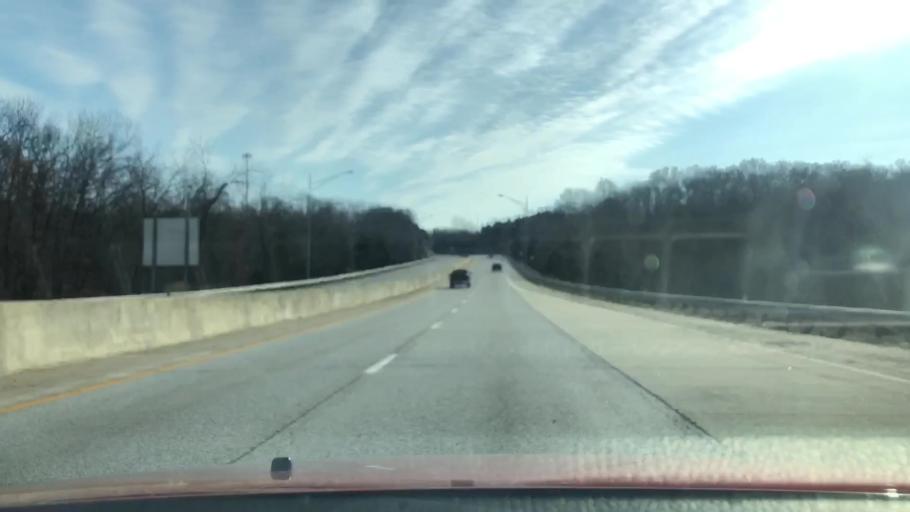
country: US
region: Missouri
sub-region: Christian County
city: Ozark
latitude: 37.1240
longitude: -93.2255
